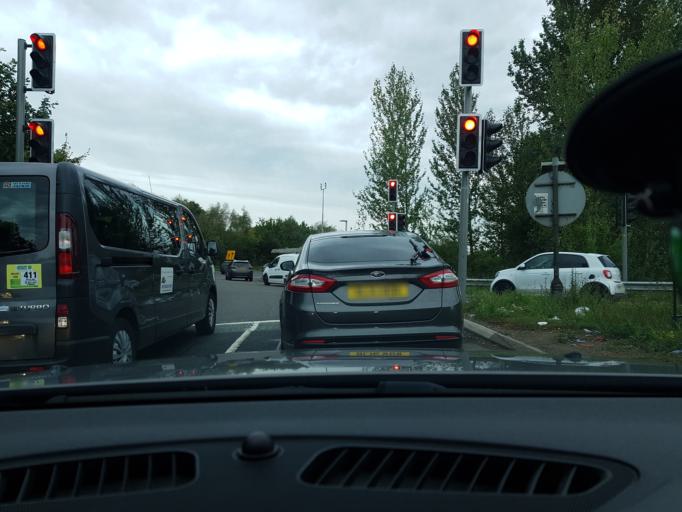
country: GB
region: England
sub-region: West Sussex
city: Copthorne
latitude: 51.1594
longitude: -0.1336
